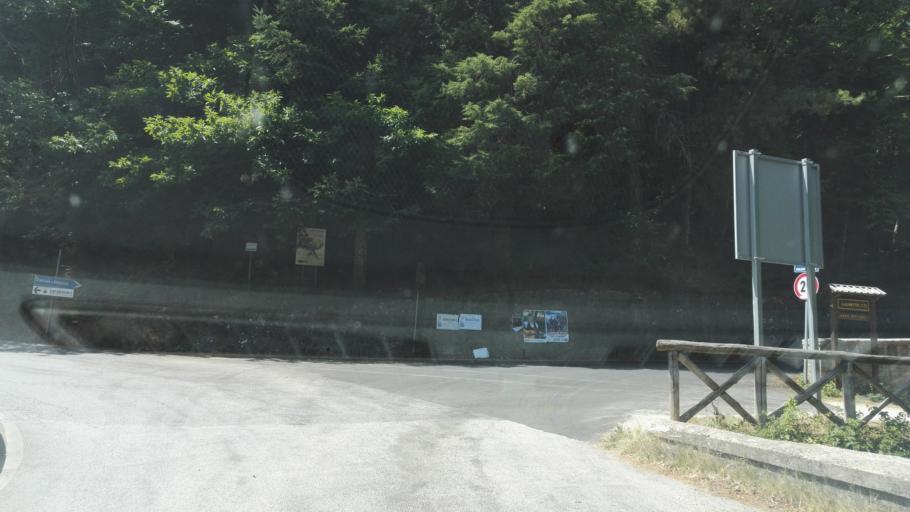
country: IT
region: Calabria
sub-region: Provincia di Vibo-Valentia
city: Mongiana
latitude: 38.5146
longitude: 16.3146
